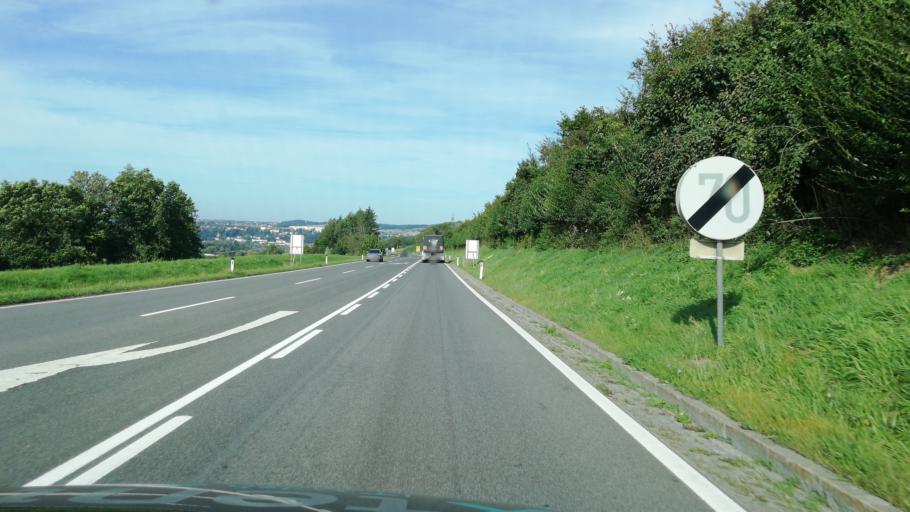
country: AT
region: Lower Austria
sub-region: Politischer Bezirk Amstetten
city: Haidershofen
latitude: 48.0445
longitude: 14.4676
